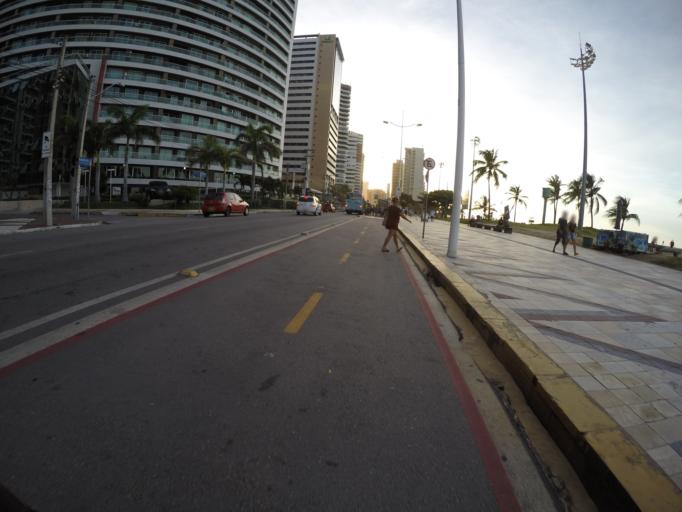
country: BR
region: Ceara
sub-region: Fortaleza
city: Fortaleza
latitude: -3.7224
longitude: -38.5078
